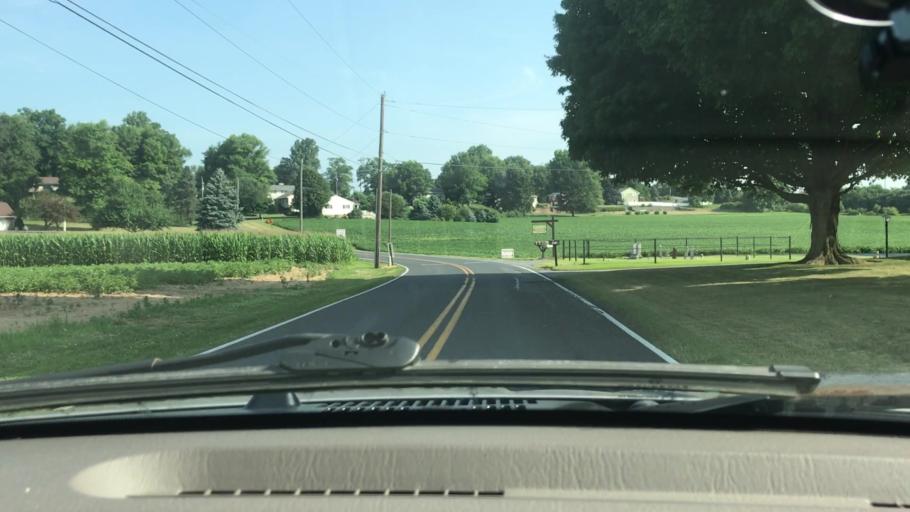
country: US
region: Pennsylvania
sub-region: Lancaster County
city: Rheems
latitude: 40.1512
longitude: -76.5719
